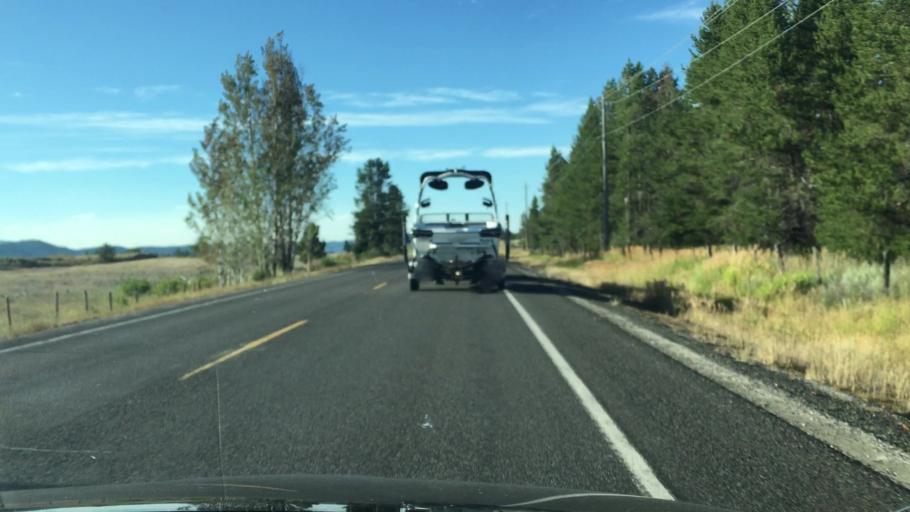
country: US
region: Idaho
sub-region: Valley County
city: Cascade
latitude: 44.4713
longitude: -115.9992
